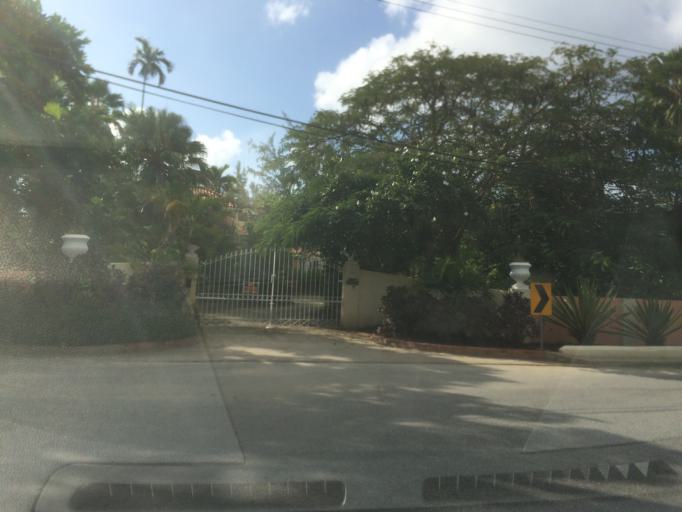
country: BB
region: Saint Peter
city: Speightstown
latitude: 13.2440
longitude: -59.6432
